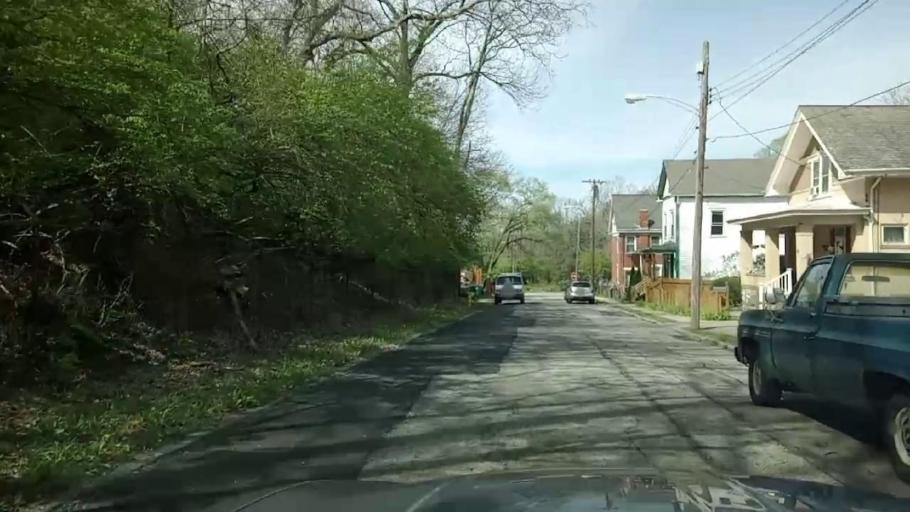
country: US
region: Kentucky
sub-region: Campbell County
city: Newport
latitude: 39.1218
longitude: -84.5120
